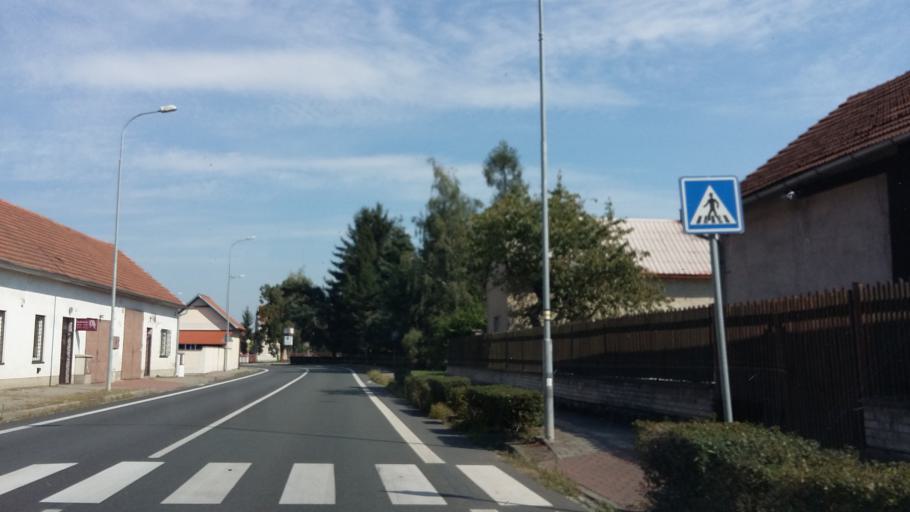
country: CZ
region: Central Bohemia
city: Velky Osek
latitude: 50.1010
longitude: 15.1862
